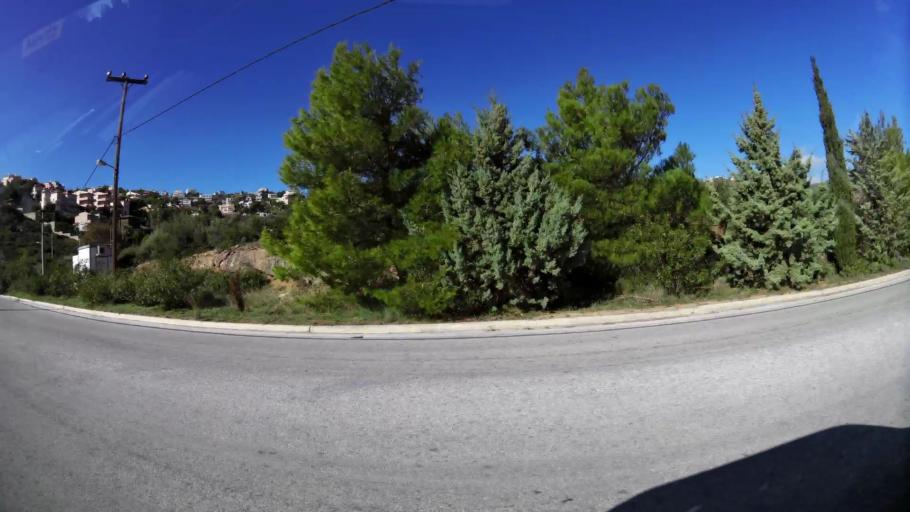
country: GR
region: Attica
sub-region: Nomarchia Anatolikis Attikis
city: Dhrafi
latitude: 38.0300
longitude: 23.9067
